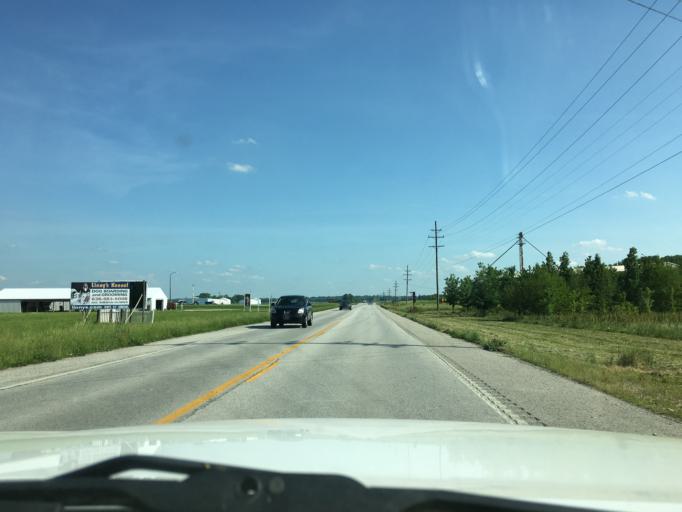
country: US
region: Missouri
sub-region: Franklin County
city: Washington
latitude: 38.5957
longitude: -91.0018
